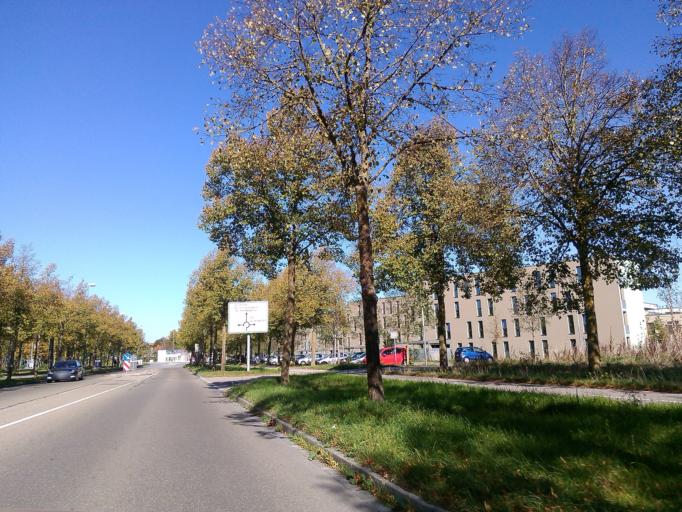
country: DE
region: Bavaria
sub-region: Swabia
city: Augsburg
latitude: 48.3262
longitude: 10.8982
